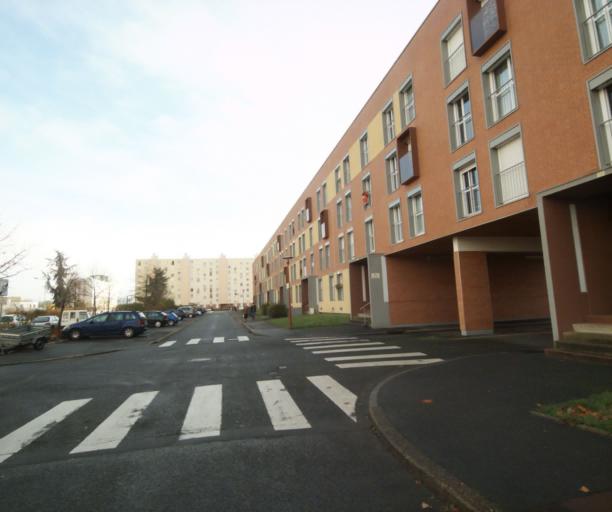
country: FR
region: Pays de la Loire
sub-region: Departement de la Sarthe
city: Le Mans
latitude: 47.9900
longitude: 0.2193
